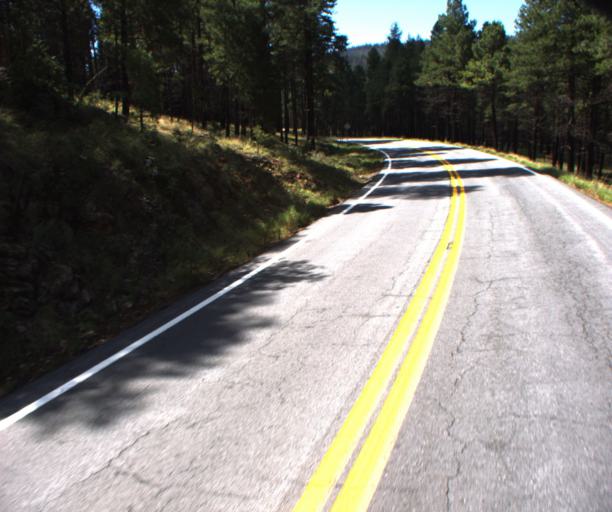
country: US
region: Arizona
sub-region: Apache County
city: Eagar
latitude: 33.7573
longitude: -109.2168
